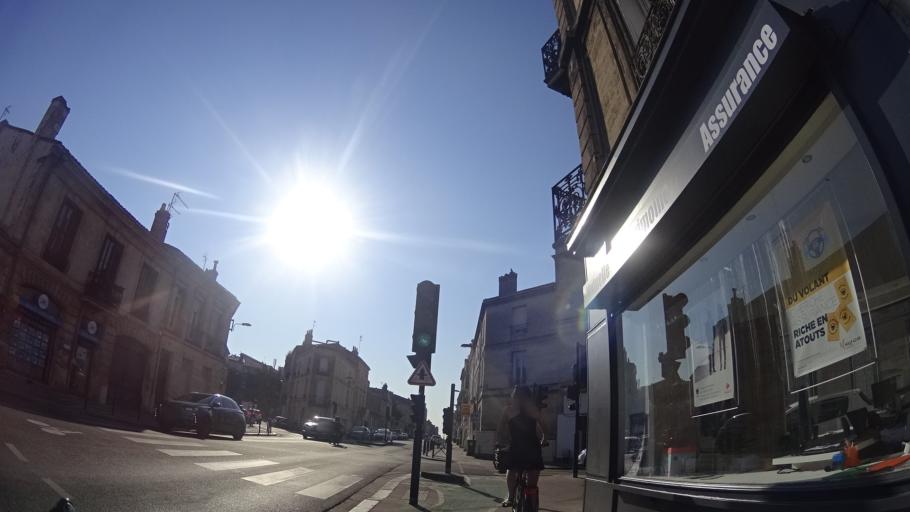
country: FR
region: Aquitaine
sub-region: Departement de la Gironde
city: Bordeaux
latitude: 44.8327
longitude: -0.5812
